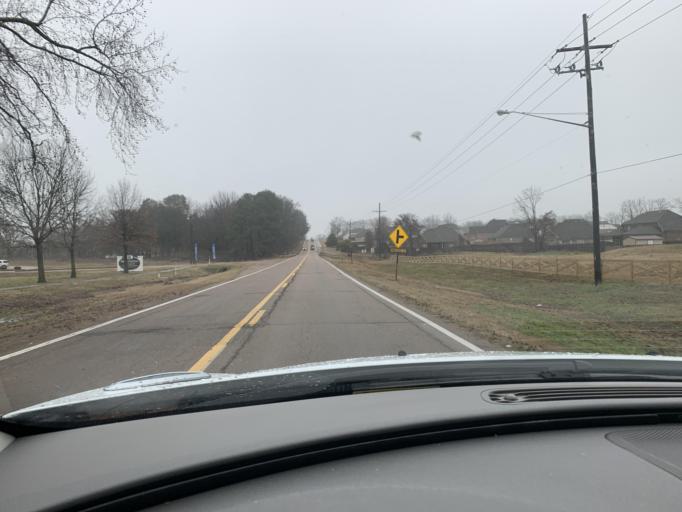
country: US
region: Mississippi
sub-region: De Soto County
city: Hernando
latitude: 34.8504
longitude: -89.9951
